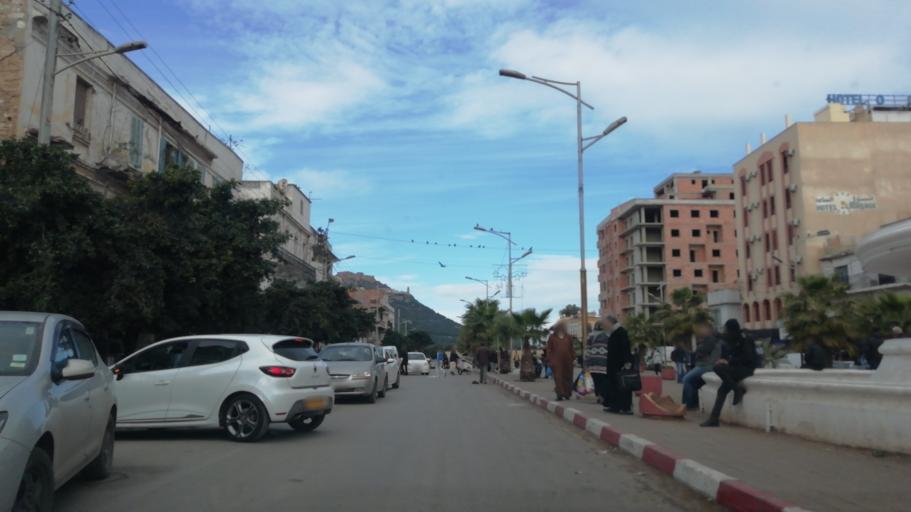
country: DZ
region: Oran
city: Oran
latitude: 35.6954
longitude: -0.6474
